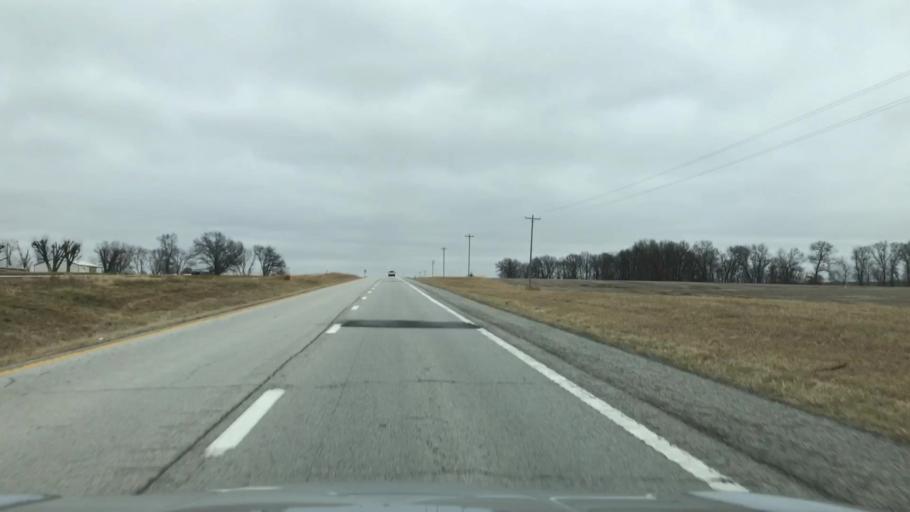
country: US
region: Missouri
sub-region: Linn County
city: Linneus
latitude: 39.7776
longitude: -93.2628
